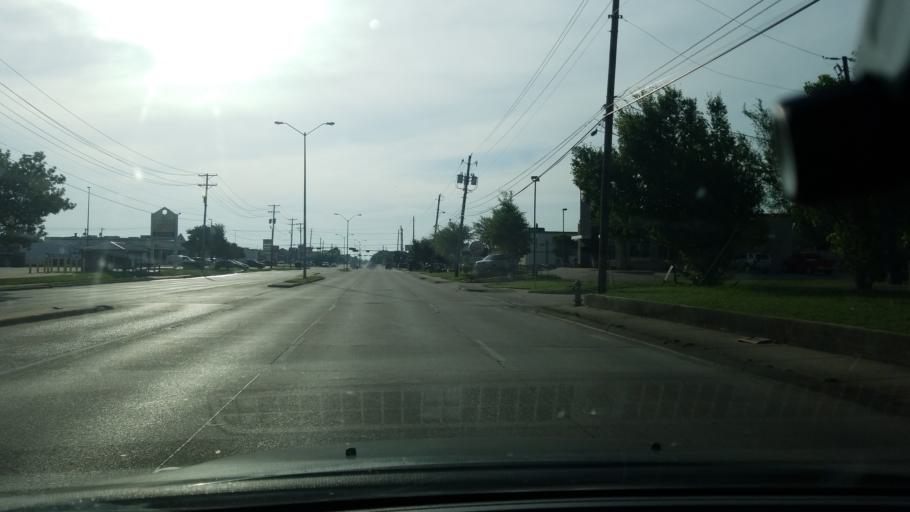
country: US
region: Texas
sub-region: Dallas County
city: Balch Springs
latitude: 32.7340
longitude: -96.6510
